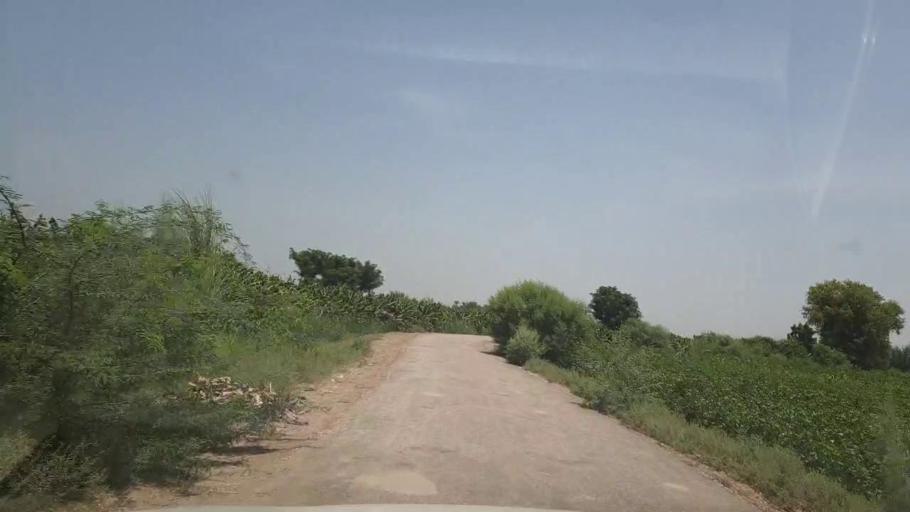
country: PK
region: Sindh
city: Bozdar
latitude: 27.1555
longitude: 68.6073
